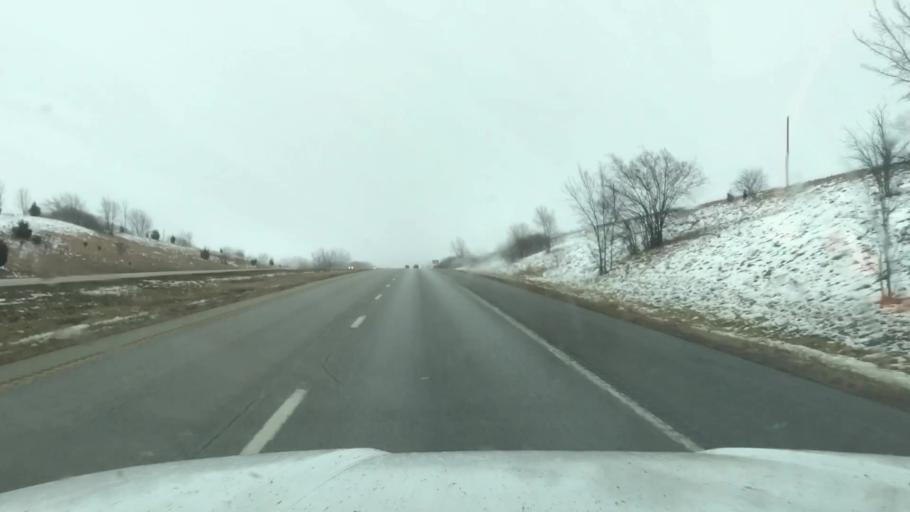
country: US
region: Missouri
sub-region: Buchanan County
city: Saint Joseph
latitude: 39.7476
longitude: -94.7072
